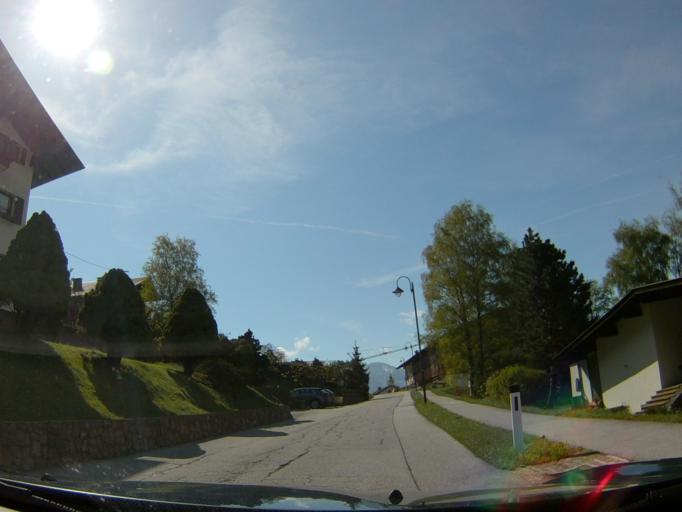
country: AT
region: Tyrol
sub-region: Politischer Bezirk Schwaz
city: Jenbach
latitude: 47.4173
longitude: 11.7578
